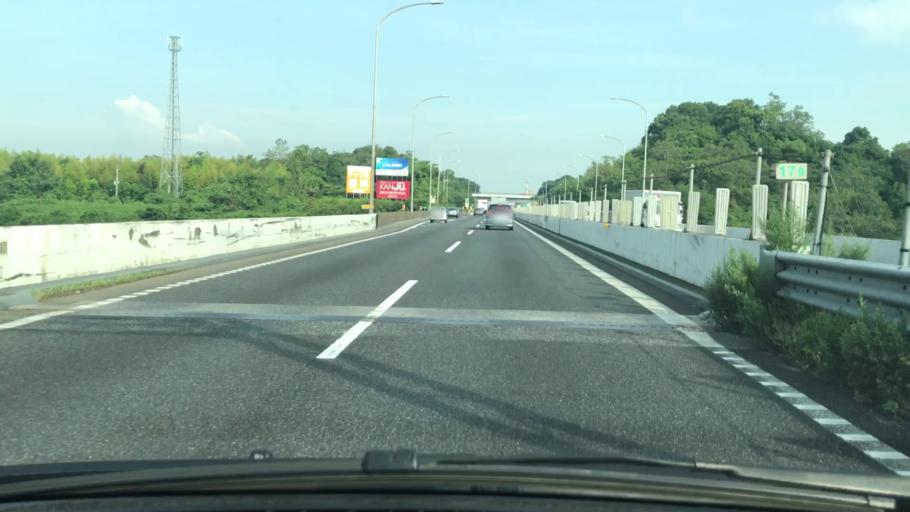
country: JP
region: Hyogo
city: Akashi
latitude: 34.7021
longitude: 134.9601
